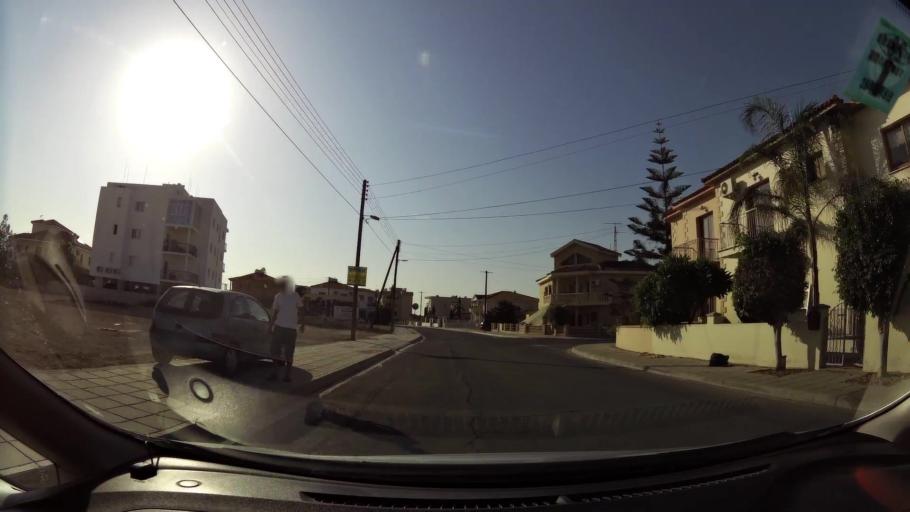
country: CY
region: Larnaka
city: Aradippou
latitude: 34.9383
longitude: 33.5968
